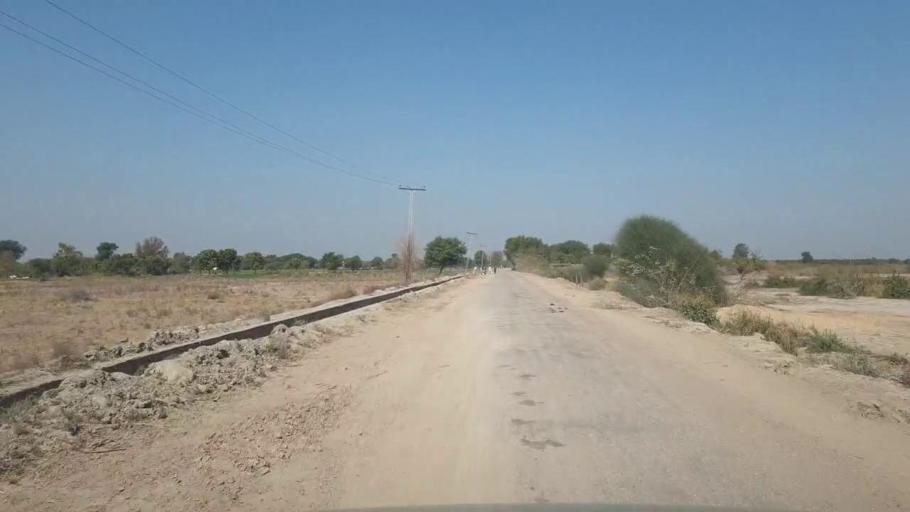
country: PK
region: Sindh
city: Chambar
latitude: 25.2939
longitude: 68.6918
